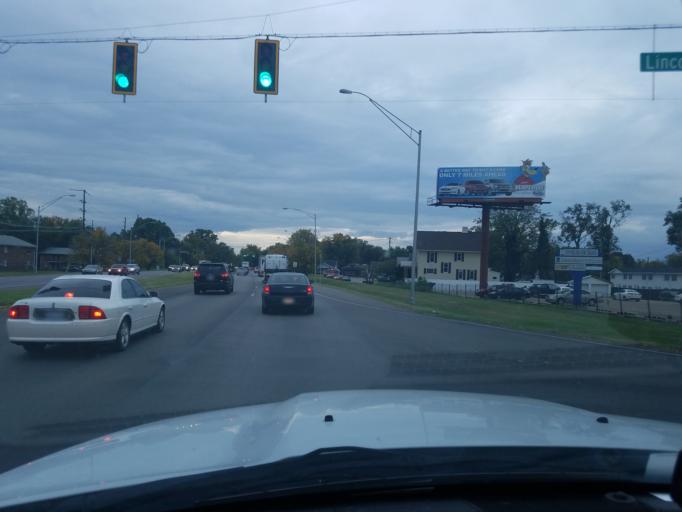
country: US
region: Indiana
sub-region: Vanderburgh County
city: Evansville
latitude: 37.9698
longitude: -87.5440
